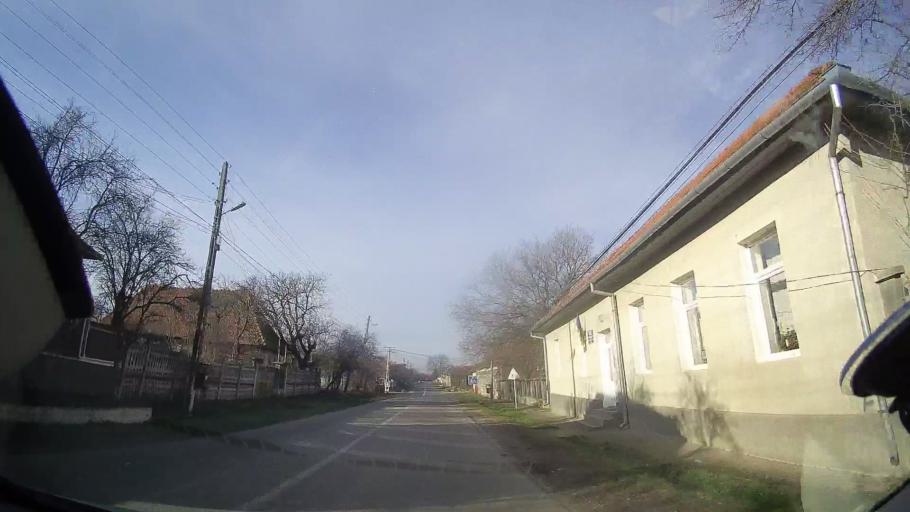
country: RO
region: Bihor
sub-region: Comuna Brusturi
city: Brusturi
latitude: 47.1436
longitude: 22.2600
